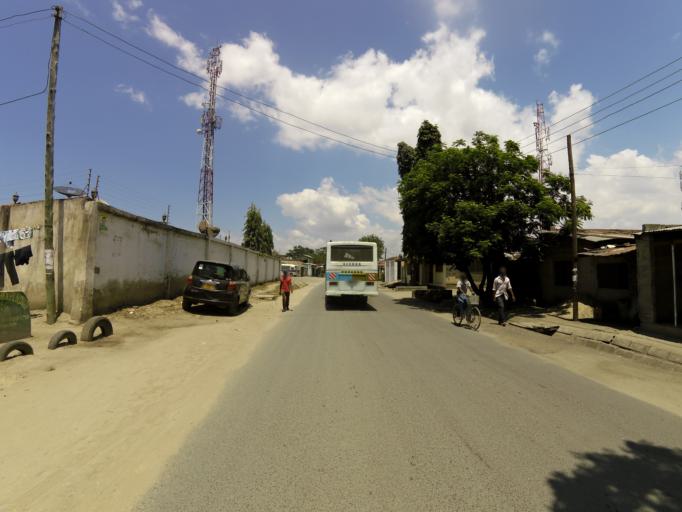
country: TZ
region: Dar es Salaam
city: Magomeni
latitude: -6.7826
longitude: 39.2506
